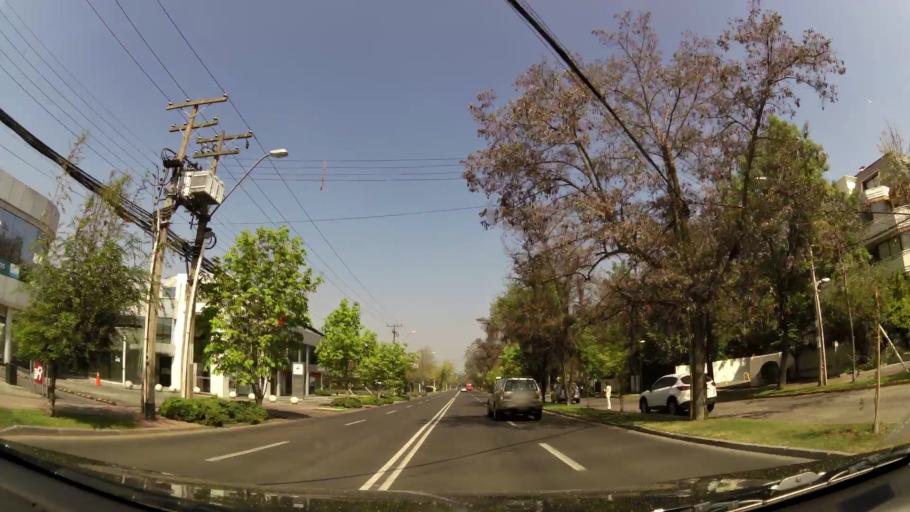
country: CL
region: Santiago Metropolitan
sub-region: Provincia de Santiago
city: Villa Presidente Frei, Nunoa, Santiago, Chile
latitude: -33.3898
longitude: -70.5787
